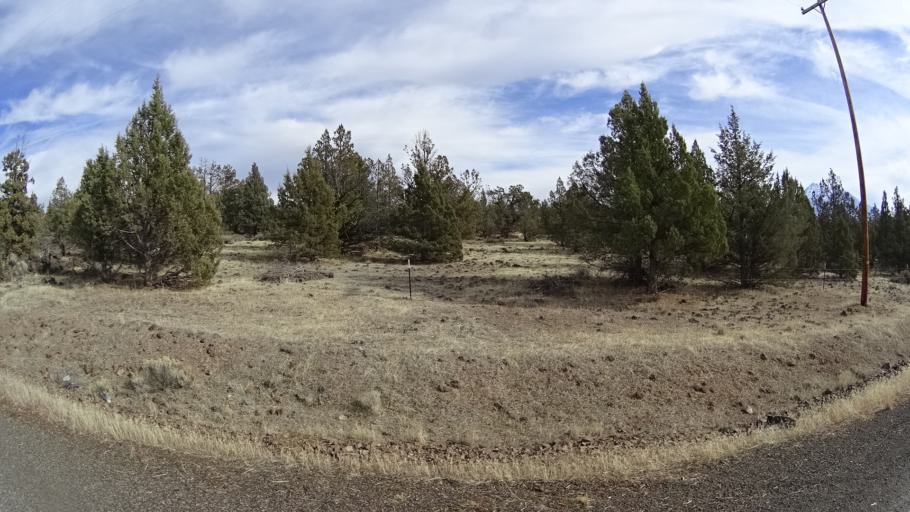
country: US
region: California
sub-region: Siskiyou County
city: Weed
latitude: 41.5982
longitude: -122.3954
